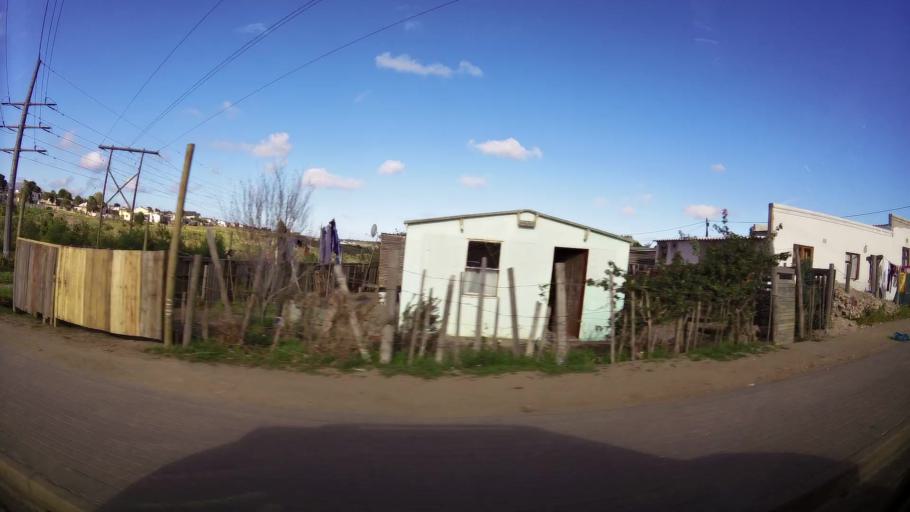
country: ZA
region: Western Cape
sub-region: Eden District Municipality
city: George
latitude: -33.9805
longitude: 22.4758
